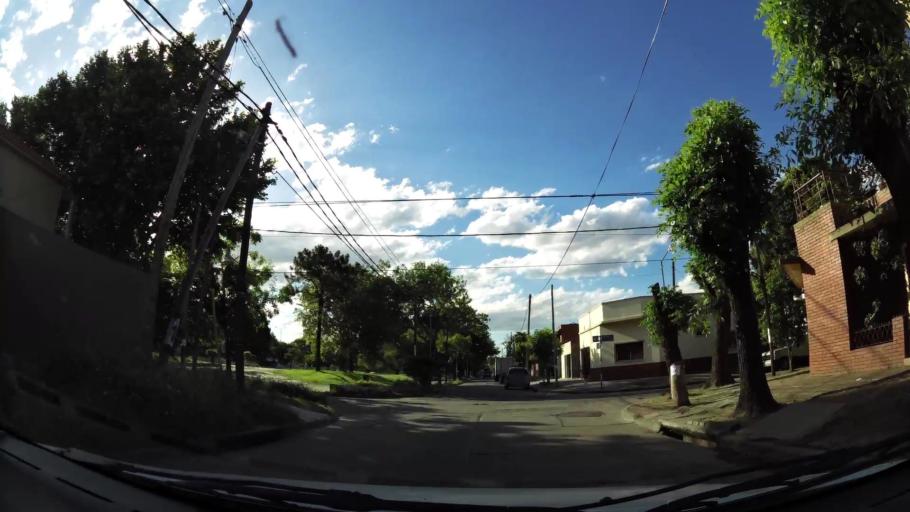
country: AR
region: Buenos Aires
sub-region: Partido de General San Martin
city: General San Martin
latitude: -34.5360
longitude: -58.5530
